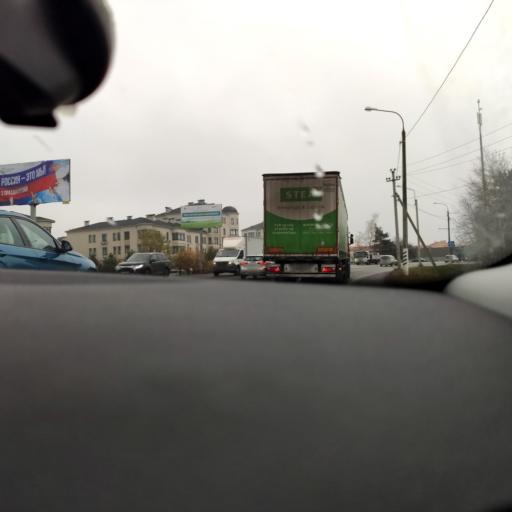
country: RU
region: Moskovskaya
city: Pavlovskaya Sloboda
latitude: 55.8122
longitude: 37.1275
